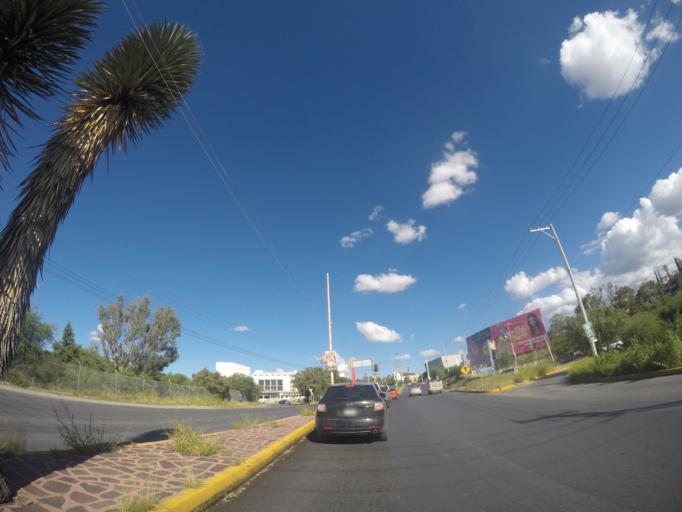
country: MX
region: San Luis Potosi
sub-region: Mexquitic de Carmona
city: Guadalupe Victoria
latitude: 22.1513
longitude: -101.0288
